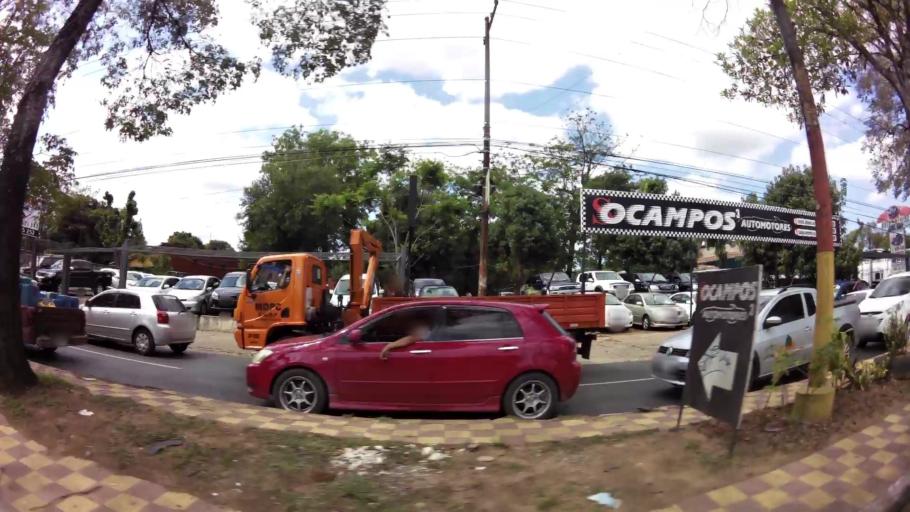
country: PY
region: Central
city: Fernando de la Mora
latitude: -25.3134
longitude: -57.5289
